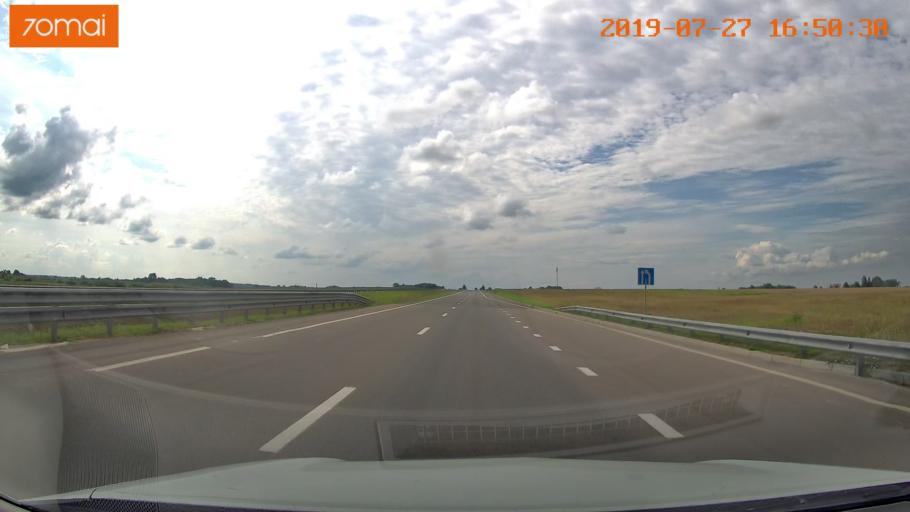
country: RU
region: Kaliningrad
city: Gvardeysk
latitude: 54.6778
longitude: 20.9123
